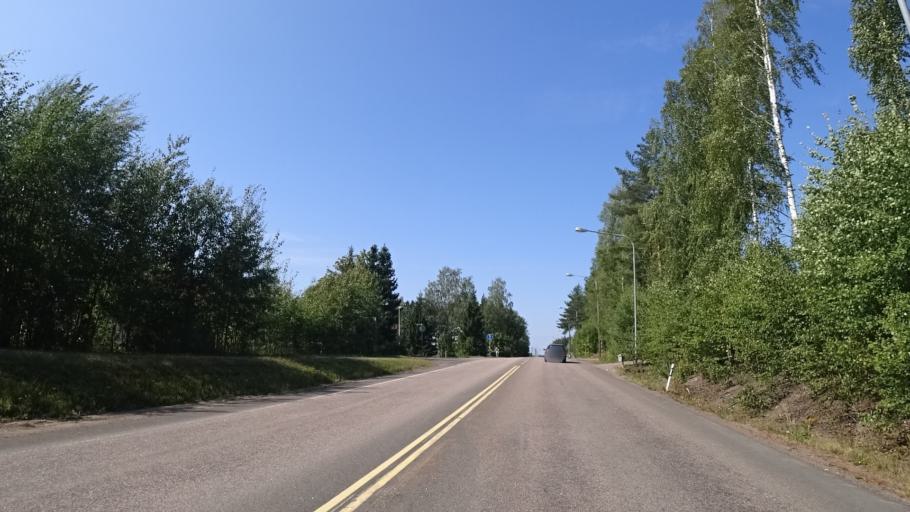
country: FI
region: Kymenlaakso
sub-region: Kotka-Hamina
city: Hamina
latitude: 60.5637
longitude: 27.1567
